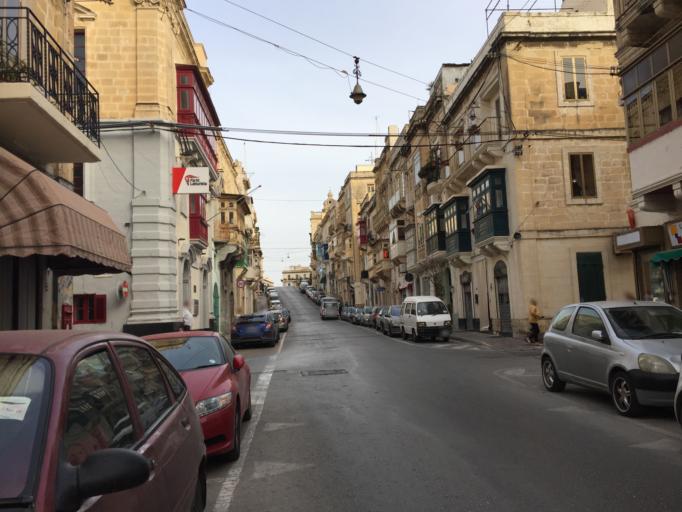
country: MT
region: L-Isla
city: Senglea
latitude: 35.8875
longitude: 14.5170
